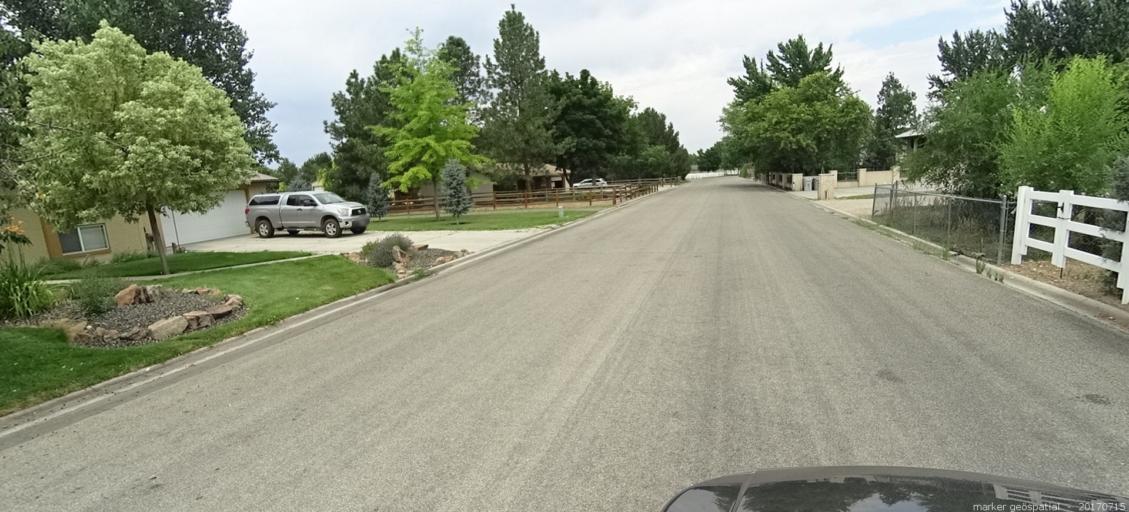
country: US
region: Idaho
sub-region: Ada County
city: Garden City
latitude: 43.5543
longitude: -116.3029
